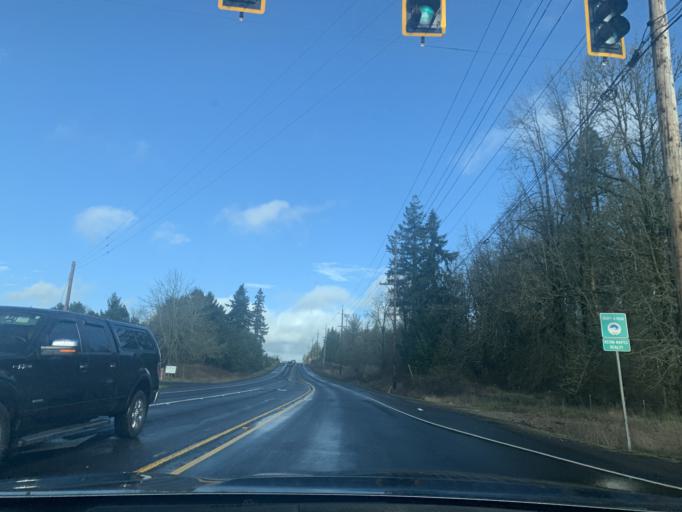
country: US
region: Oregon
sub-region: Washington County
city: Sherwood
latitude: 45.4005
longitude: -122.8517
